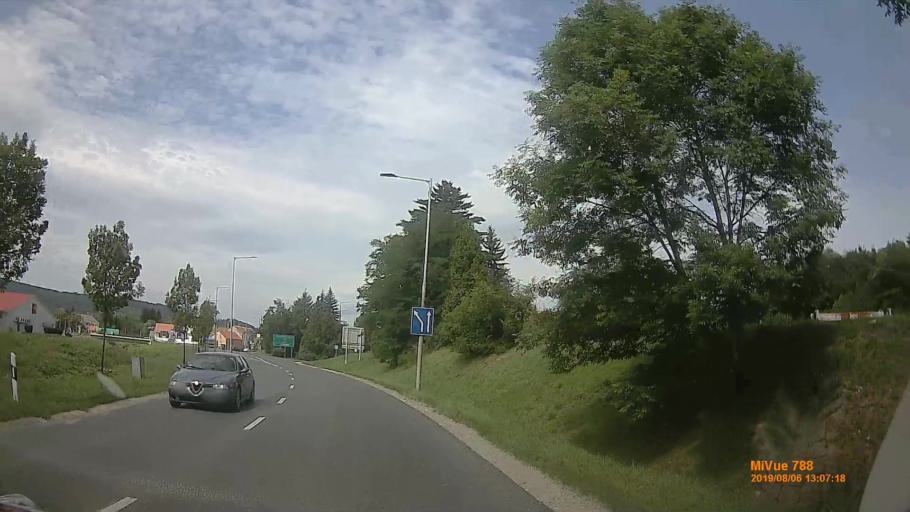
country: HU
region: Vas
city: Koszeg
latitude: 47.3803
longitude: 16.5573
